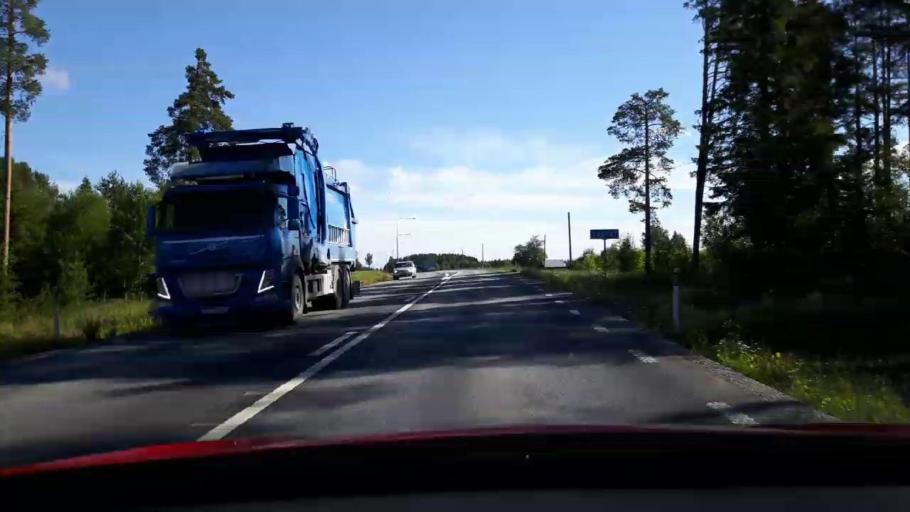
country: SE
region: Jaemtland
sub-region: OEstersunds Kommun
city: Lit
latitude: 63.2344
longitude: 14.7675
